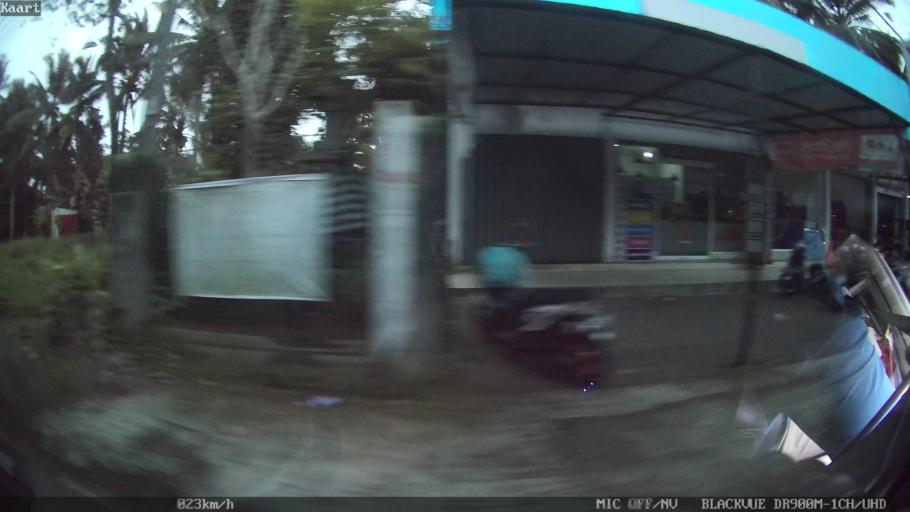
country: ID
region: Bali
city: Banjar Buahan
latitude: -8.4123
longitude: 115.2444
